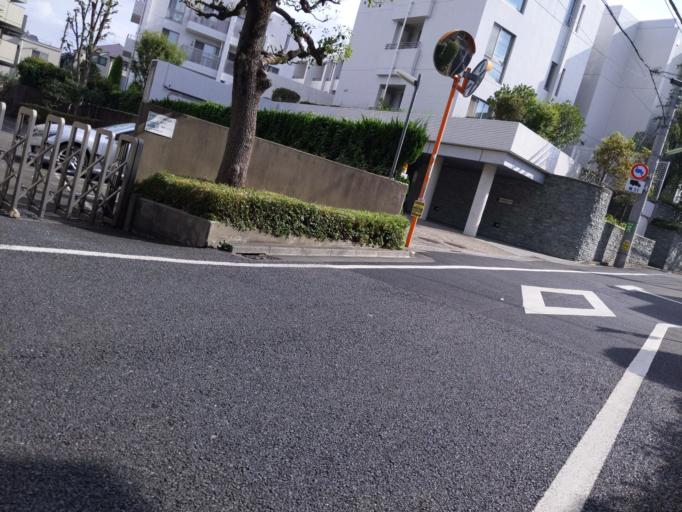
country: JP
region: Tokyo
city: Mitaka-shi
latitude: 35.6521
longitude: 139.6260
